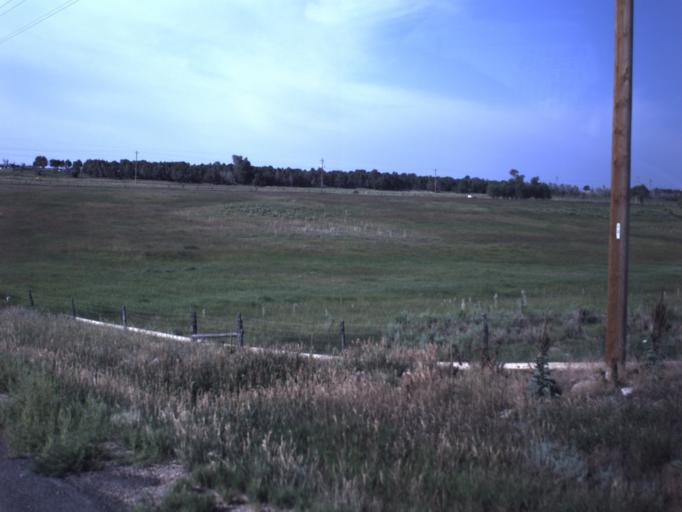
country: US
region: Utah
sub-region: Duchesne County
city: Duchesne
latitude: 40.3345
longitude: -110.4079
